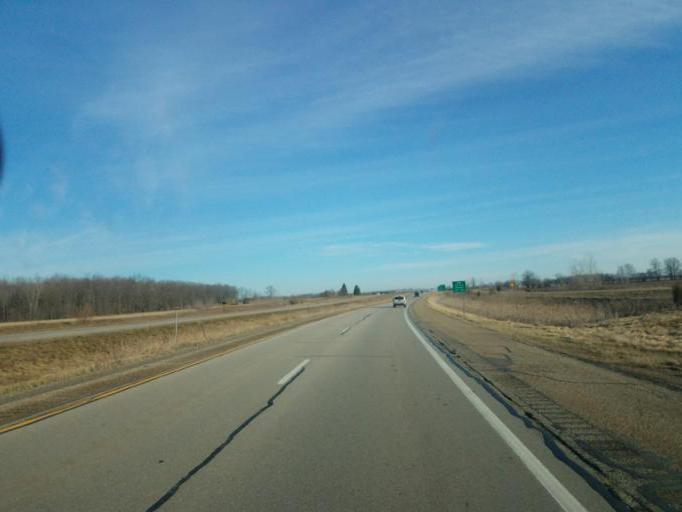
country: US
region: Michigan
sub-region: Gratiot County
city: Ithaca
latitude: 43.1657
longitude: -84.5635
